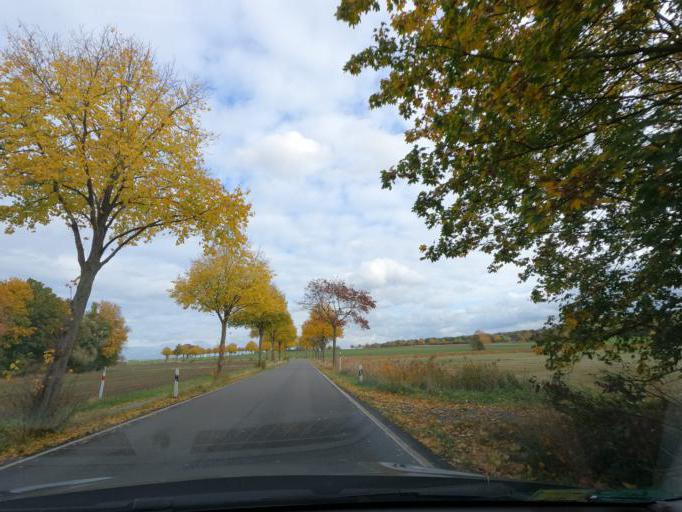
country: DE
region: Lower Saxony
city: Leiferde
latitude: 52.1965
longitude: 10.4805
